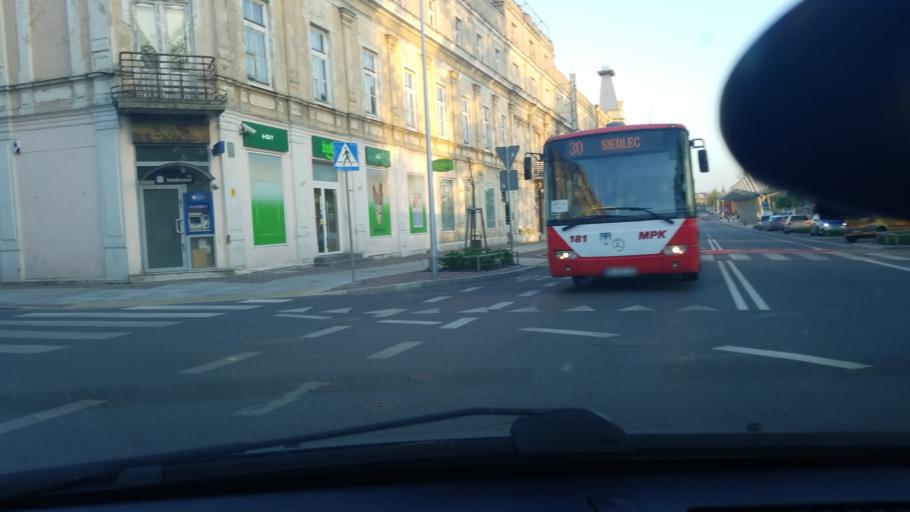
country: PL
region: Silesian Voivodeship
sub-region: Czestochowa
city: Czestochowa
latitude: 50.8108
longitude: 19.1222
